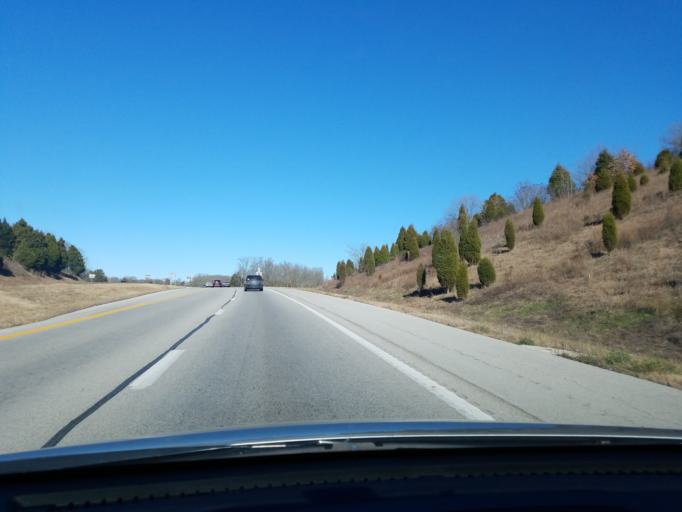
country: US
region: Missouri
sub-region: Taney County
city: Merriam Woods
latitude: 36.7903
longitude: -93.2247
